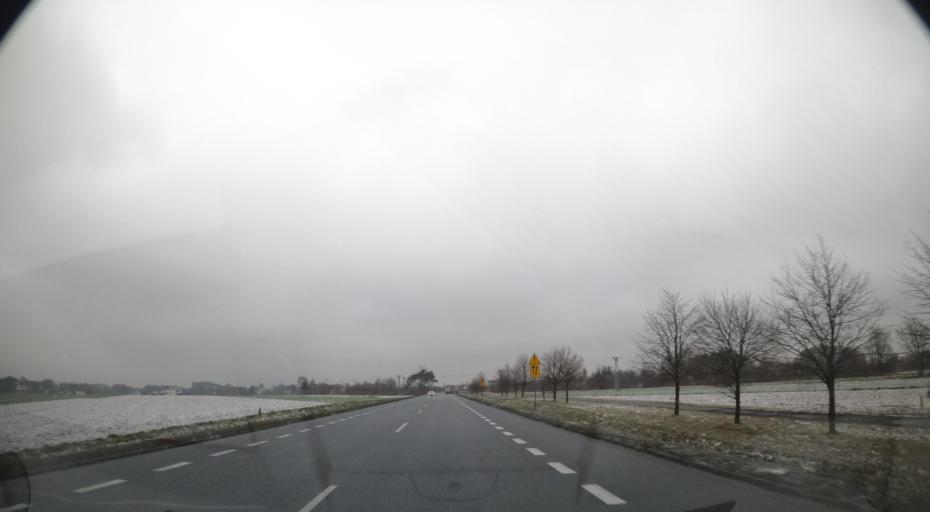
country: PL
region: Masovian Voivodeship
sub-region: Powiat sochaczewski
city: Sochaczew
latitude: 52.2068
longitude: 20.2417
